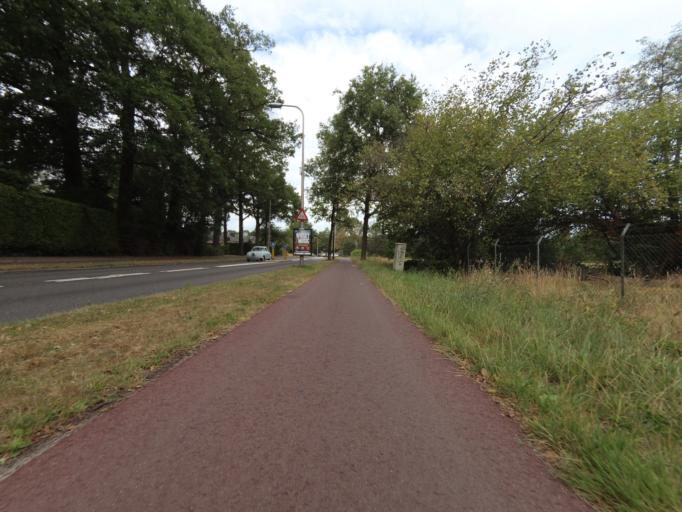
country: NL
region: Overijssel
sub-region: Gemeente Enschede
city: Enschede
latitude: 52.2246
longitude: 6.9289
